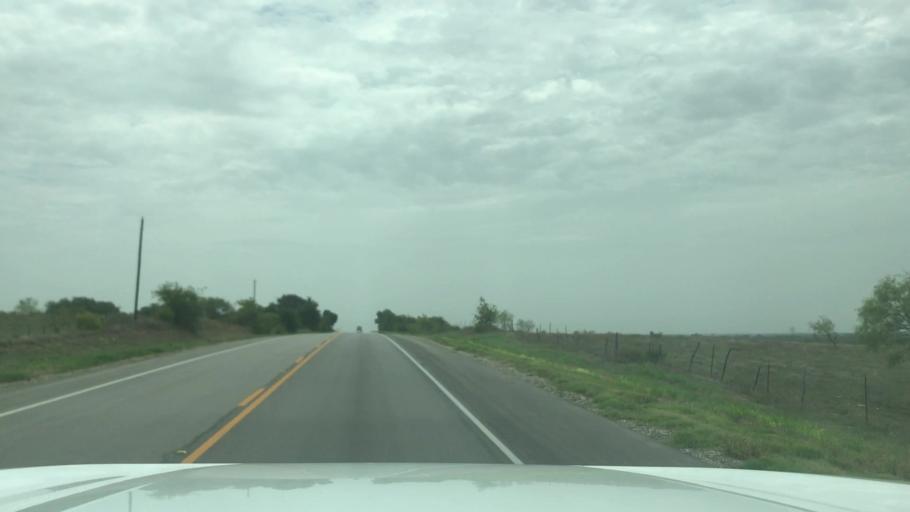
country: US
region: Texas
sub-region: Erath County
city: Dublin
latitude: 32.0811
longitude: -98.2452
